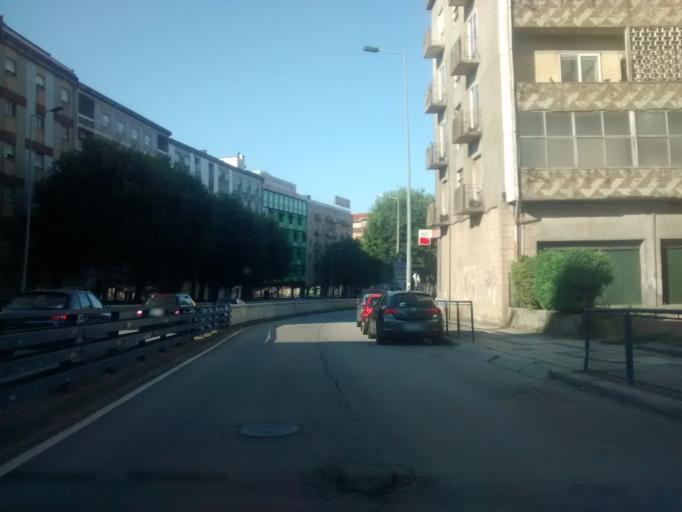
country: PT
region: Braga
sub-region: Braga
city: Braga
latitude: 41.5469
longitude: -8.4183
